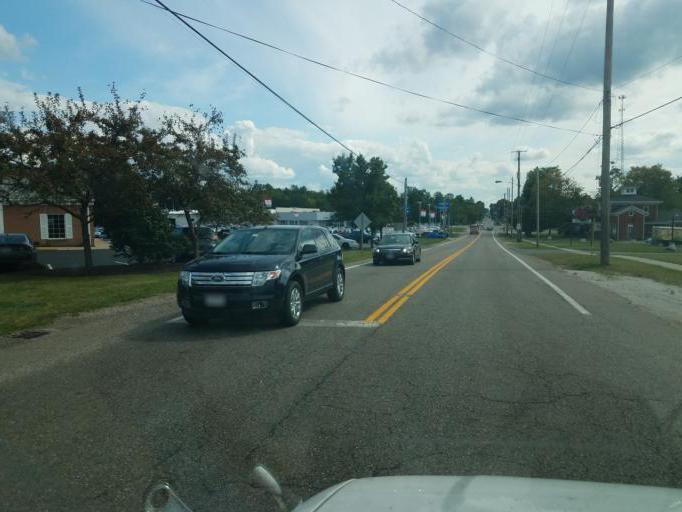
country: US
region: Ohio
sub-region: Stark County
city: Hartville
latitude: 41.0329
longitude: -81.2482
